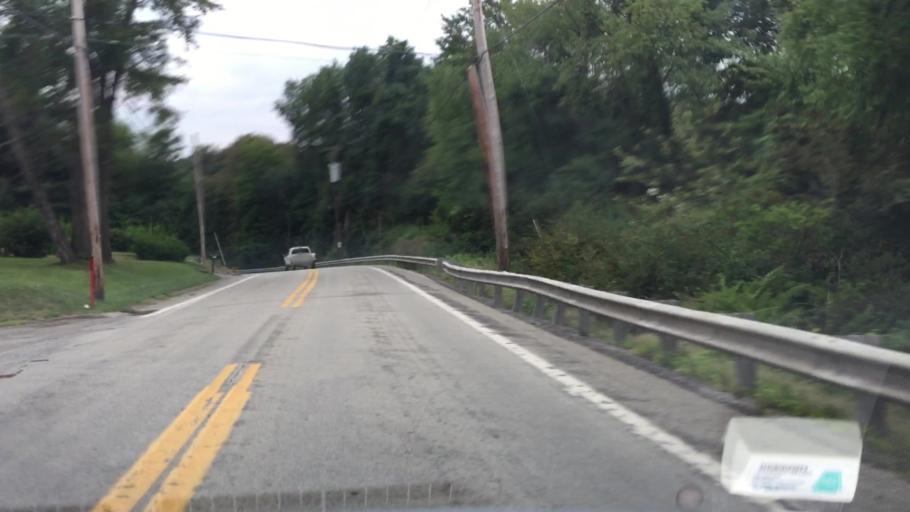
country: US
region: Pennsylvania
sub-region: Allegheny County
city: Curtisville
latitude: 40.6187
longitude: -79.8679
